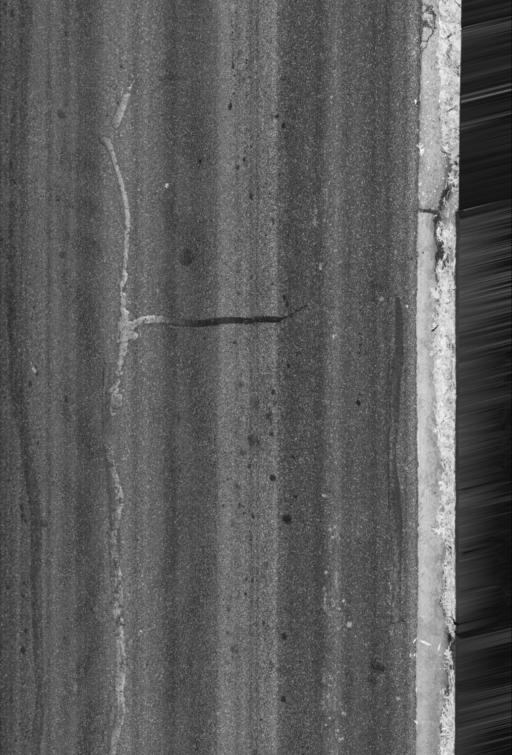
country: US
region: Maryland
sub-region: Montgomery County
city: Friendship Village
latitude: 38.9322
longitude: -77.0781
